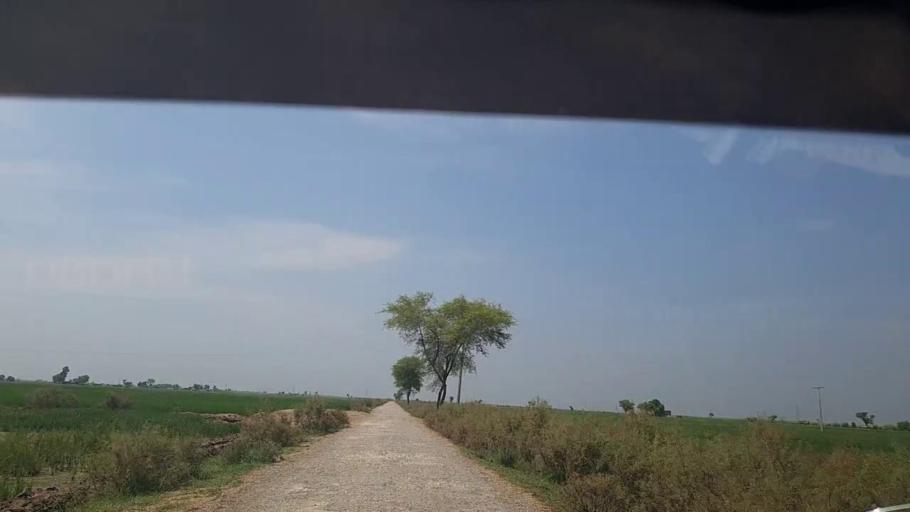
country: PK
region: Sindh
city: Thul
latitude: 28.2144
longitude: 68.6825
